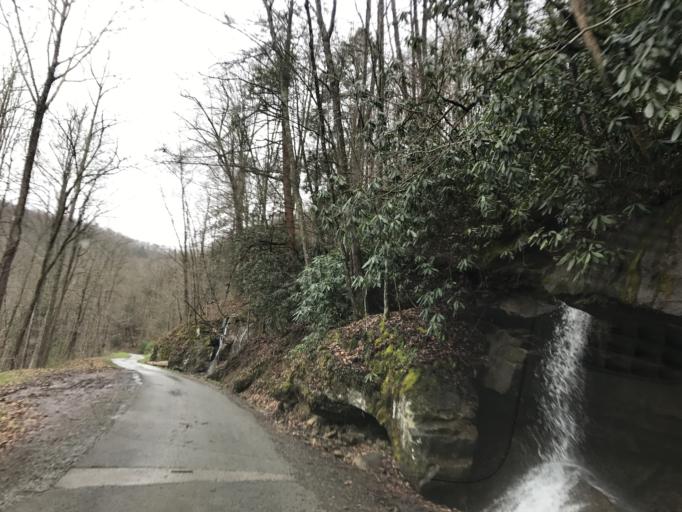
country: US
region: West Virginia
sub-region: Fayette County
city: Fayetteville
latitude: 38.0635
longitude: -81.0827
